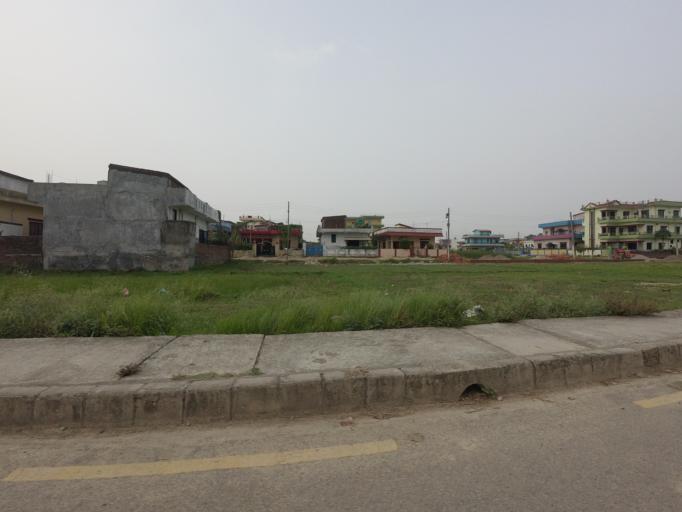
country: NP
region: Western Region
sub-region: Lumbini Zone
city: Bhairahawa
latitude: 27.5217
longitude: 83.4453
